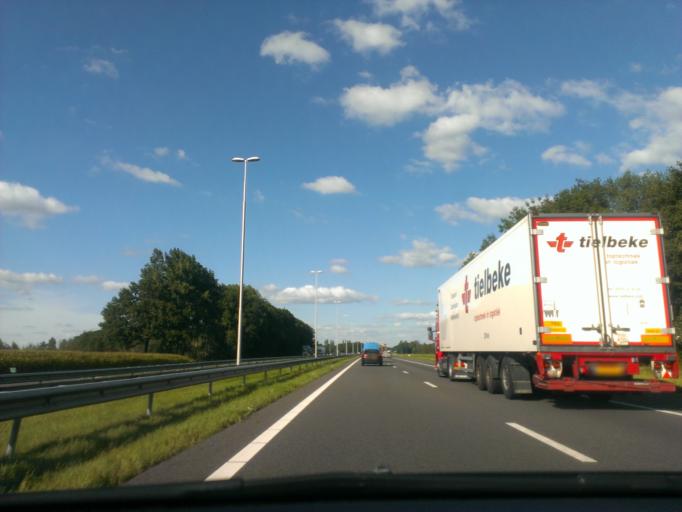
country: NL
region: Gelderland
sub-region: Gemeente Epe
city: Oene
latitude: 52.3486
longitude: 6.0176
